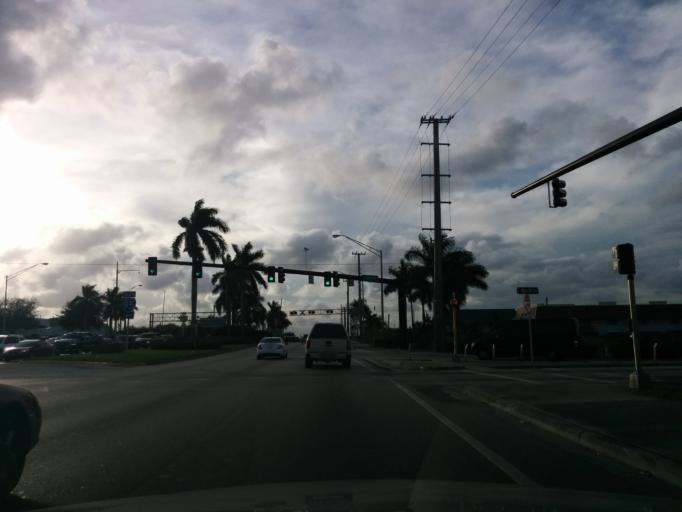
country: US
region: Florida
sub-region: Broward County
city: Dania Beach
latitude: 26.0629
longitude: -80.1642
